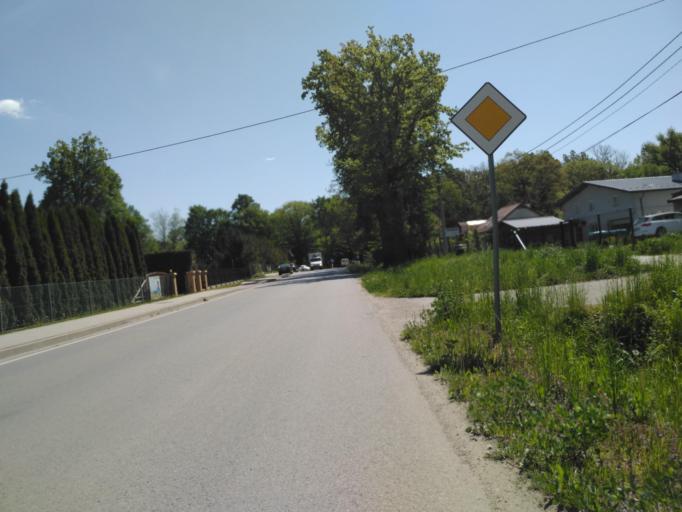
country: PL
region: Subcarpathian Voivodeship
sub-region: Powiat krosnienski
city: Miejsce Piastowe
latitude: 49.6032
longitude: 21.7959
